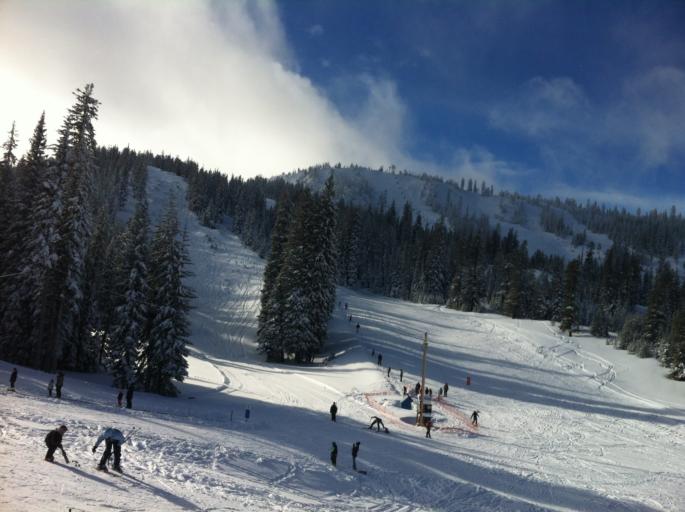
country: US
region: Oregon
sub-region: Union County
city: La Grande
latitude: 44.9629
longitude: -118.2337
